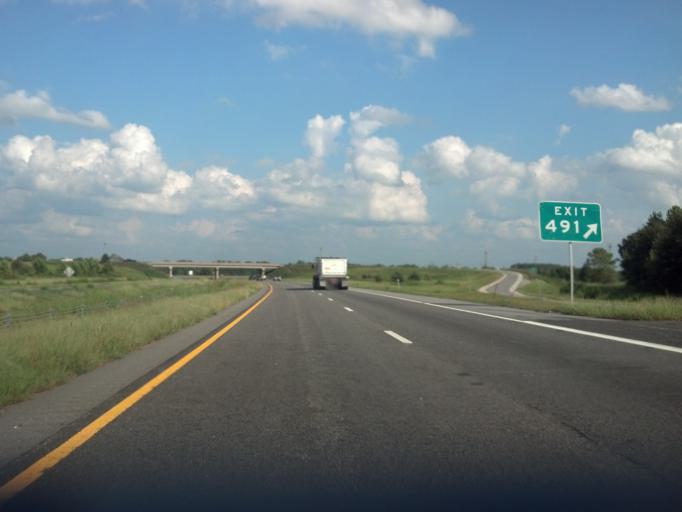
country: US
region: North Carolina
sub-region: Edgecombe County
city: Princeville
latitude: 35.8551
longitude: -77.4654
